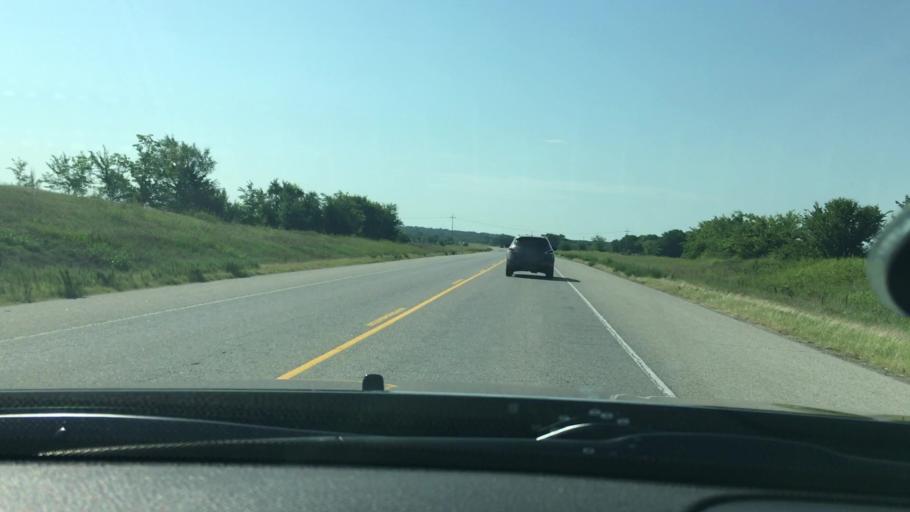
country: US
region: Oklahoma
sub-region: Pontotoc County
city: Ada
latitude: 34.7137
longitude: -96.6206
